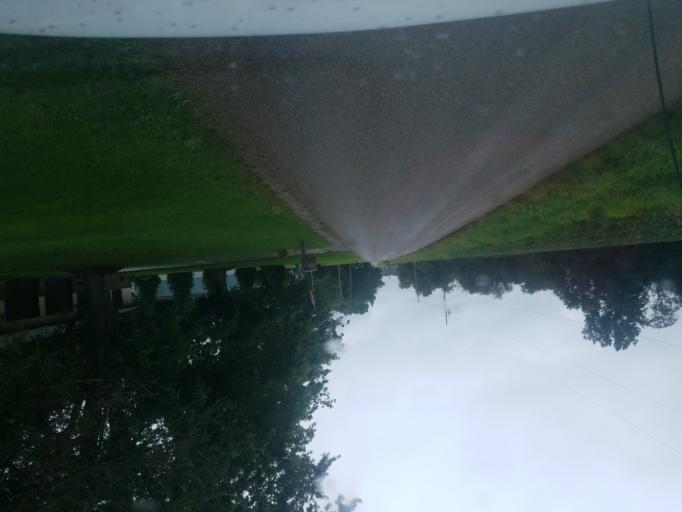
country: US
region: Ohio
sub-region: Wayne County
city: West Salem
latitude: 40.9089
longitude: -82.1184
